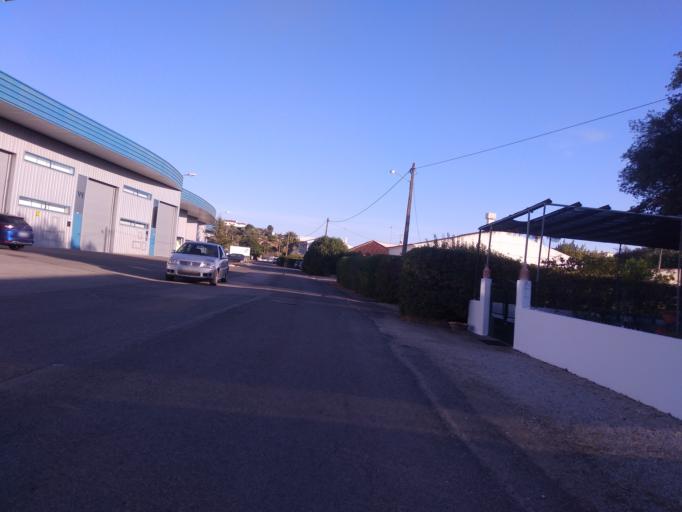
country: PT
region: Faro
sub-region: Sao Bras de Alportel
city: Sao Bras de Alportel
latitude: 37.1687
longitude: -7.8934
